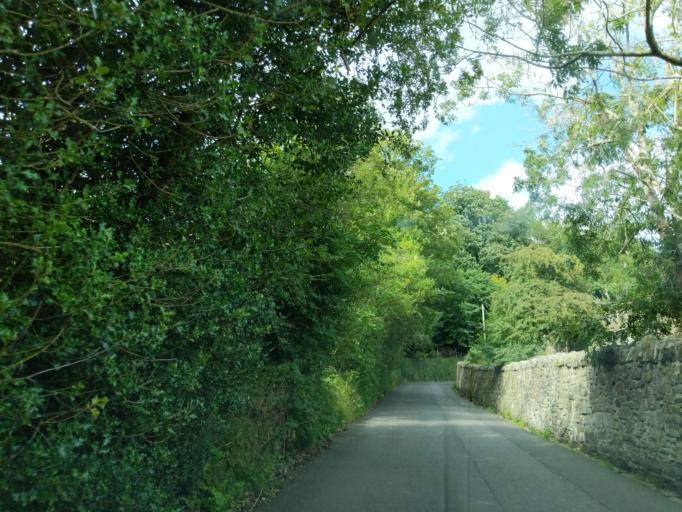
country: GB
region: Scotland
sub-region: Midlothian
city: Loanhead
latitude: 55.8725
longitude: -3.1450
